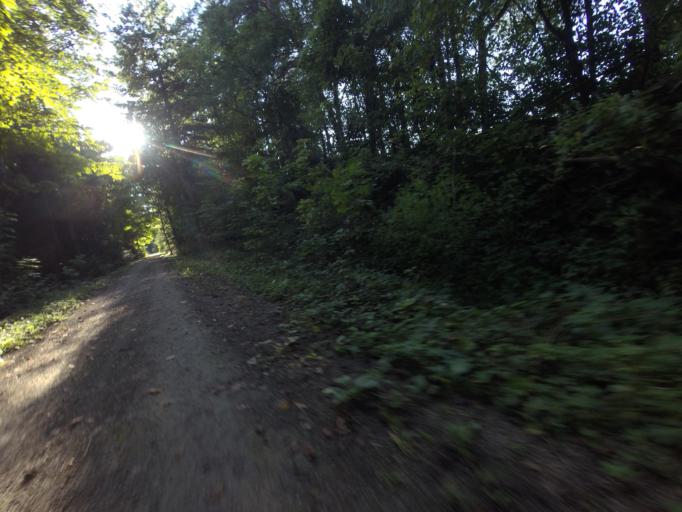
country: CA
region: Ontario
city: Goderich
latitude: 43.7520
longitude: -81.6205
